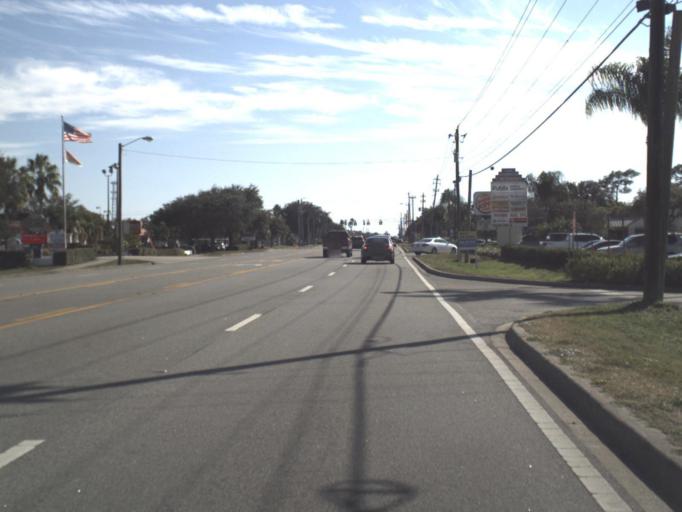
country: US
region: Florida
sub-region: Brevard County
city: June Park
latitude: 28.1491
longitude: -80.6719
